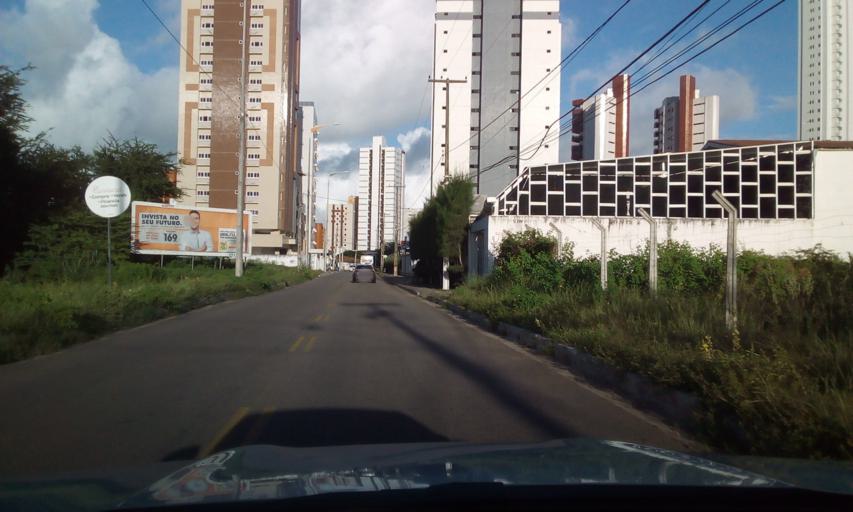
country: BR
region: Paraiba
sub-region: Joao Pessoa
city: Joao Pessoa
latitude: -7.0932
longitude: -34.8453
